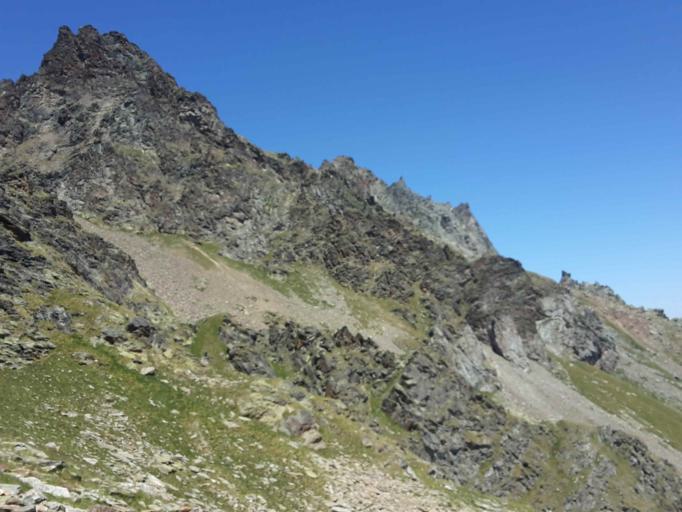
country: IT
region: Aosta Valley
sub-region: Valle d'Aosta
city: Valgrisenche
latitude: 45.6826
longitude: 7.0523
